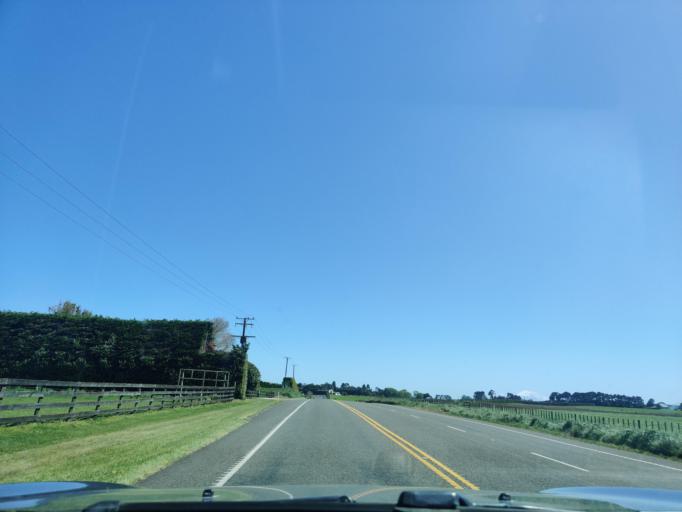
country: NZ
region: Taranaki
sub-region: South Taranaki District
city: Patea
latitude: -39.7661
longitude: 174.6498
